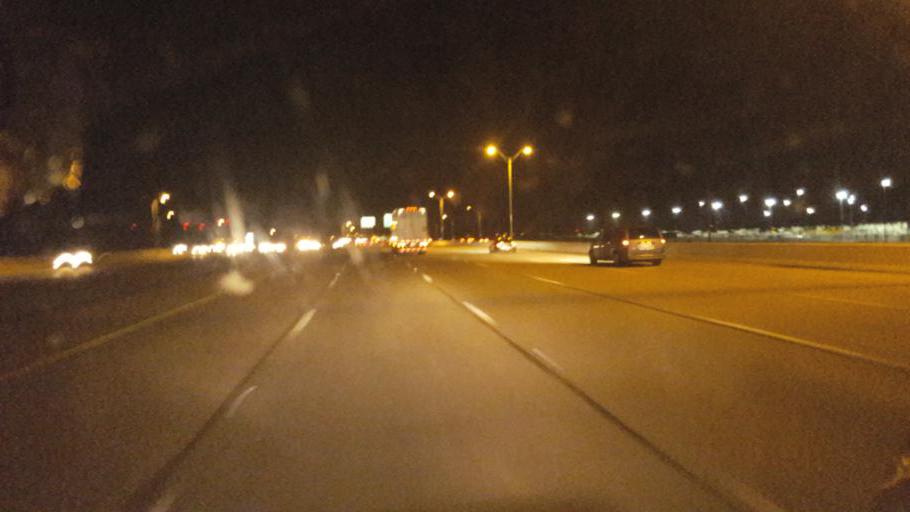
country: US
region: Indiana
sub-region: Marion County
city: Speedway
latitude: 39.7084
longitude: -86.2838
